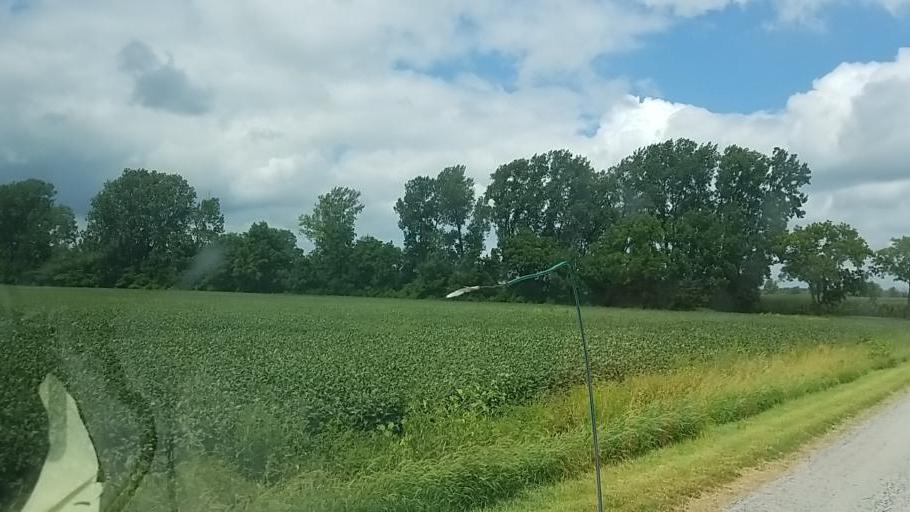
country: US
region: Ohio
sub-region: Clark County
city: South Charleston
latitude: 39.8226
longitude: -83.7209
